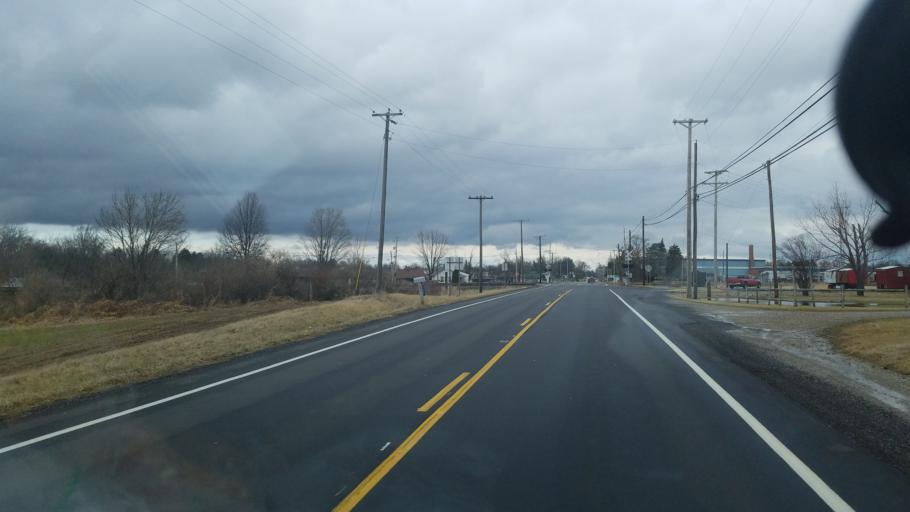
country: US
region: Ohio
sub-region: Crawford County
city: Galion
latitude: 40.7188
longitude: -82.8099
